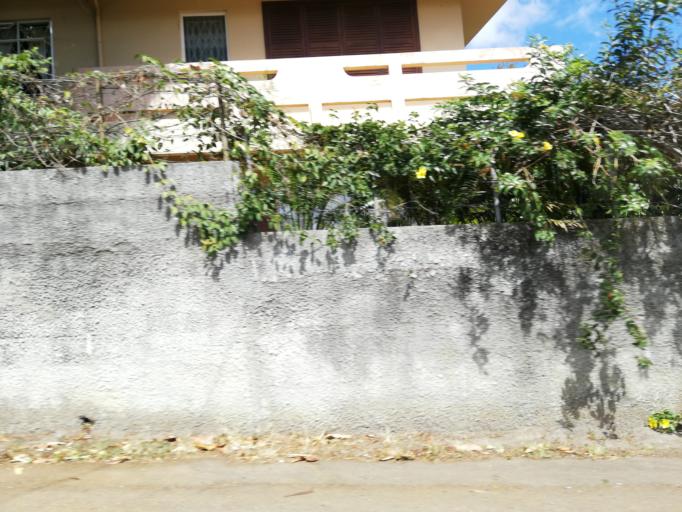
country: MU
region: Plaines Wilhems
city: Ebene
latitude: -20.2361
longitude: 57.4645
